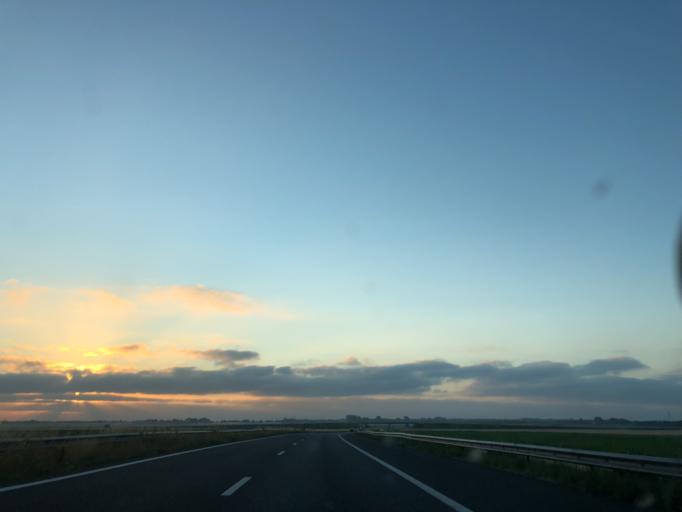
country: NL
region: Groningen
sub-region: Gemeente  Oldambt
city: Winschoten
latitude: 53.1881
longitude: 6.9517
